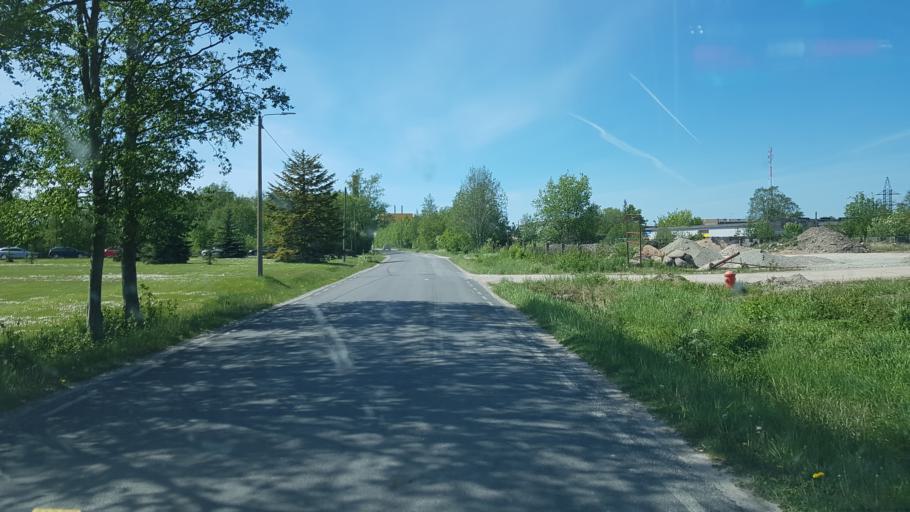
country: EE
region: Saare
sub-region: Kuressaare linn
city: Kuressaare
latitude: 58.2721
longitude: 22.4950
